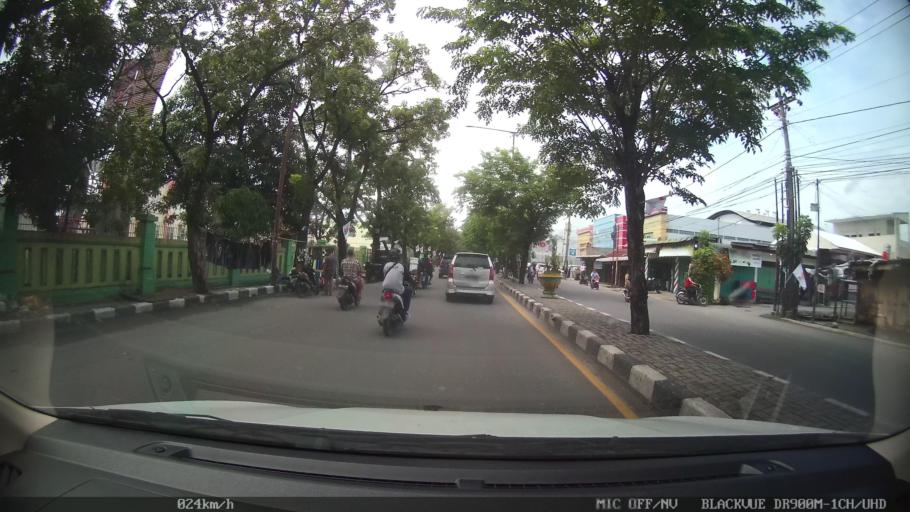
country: ID
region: North Sumatra
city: Medan
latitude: 3.6143
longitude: 98.7073
